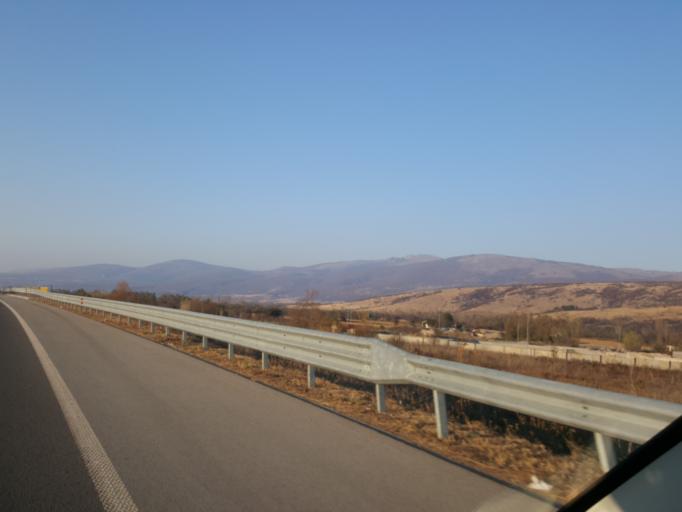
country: RS
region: Central Serbia
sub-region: Pirotski Okrug
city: Dimitrovgrad
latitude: 43.0677
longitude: 22.6787
